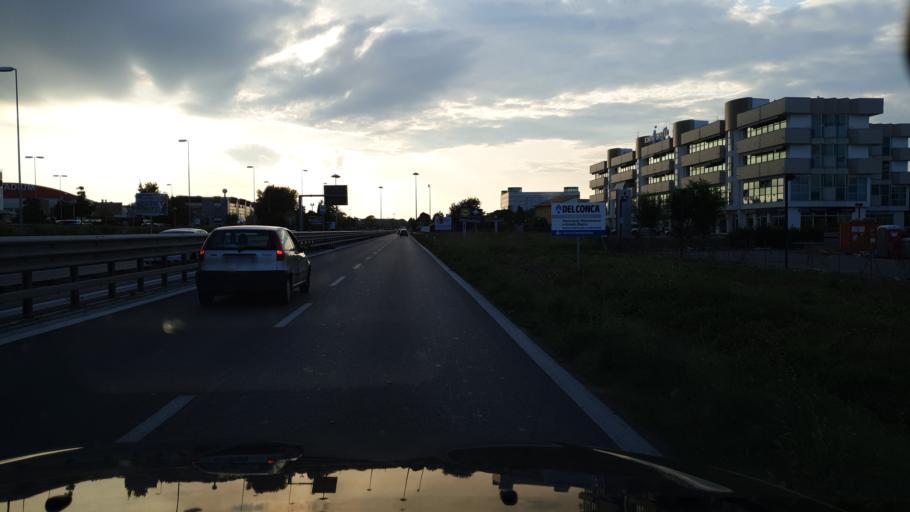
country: IT
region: Emilia-Romagna
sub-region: Provincia di Rimini
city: Rivazzurra
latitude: 44.0413
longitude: 12.5869
